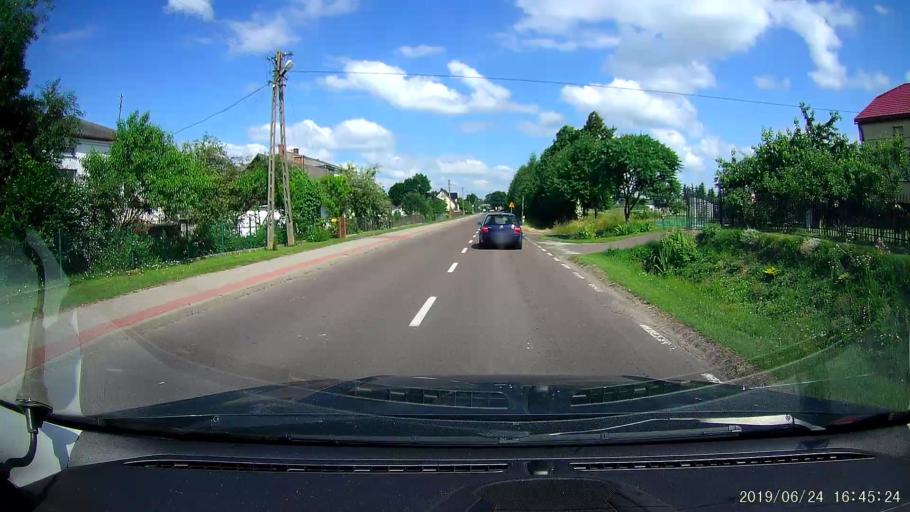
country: PL
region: Lublin Voivodeship
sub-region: Powiat tomaszowski
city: Laszczow
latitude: 50.5324
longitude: 23.6675
